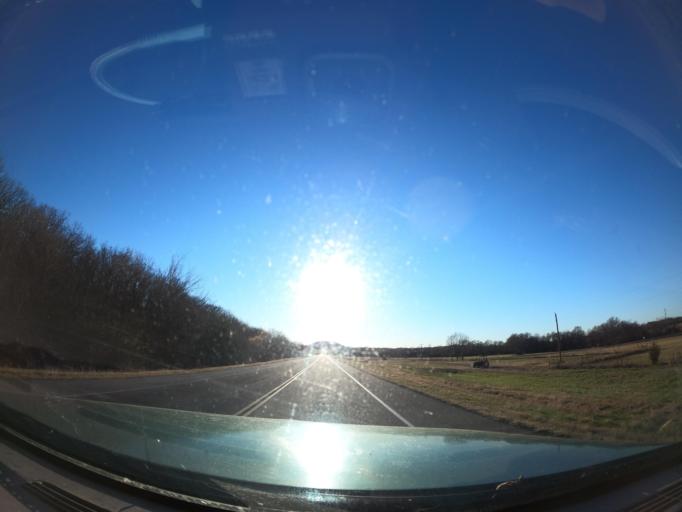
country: US
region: Oklahoma
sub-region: Pittsburg County
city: Hartshorne
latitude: 34.8707
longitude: -95.5162
